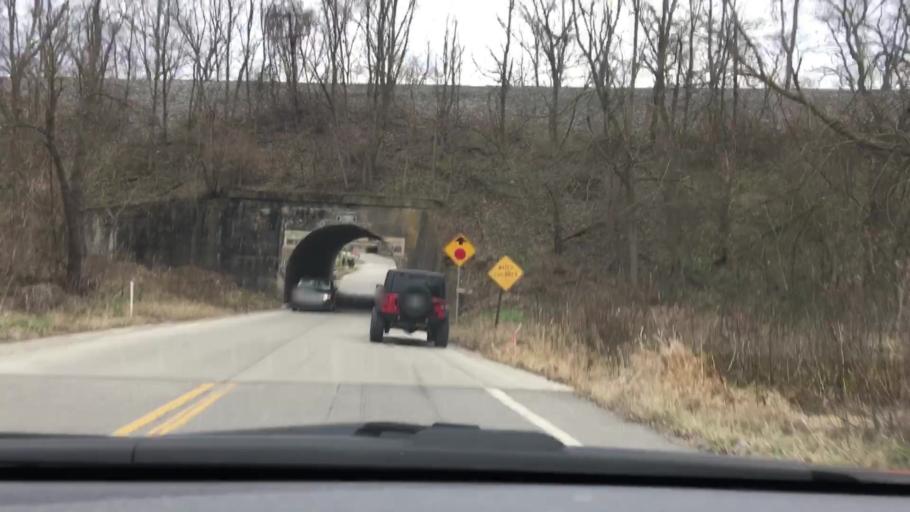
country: US
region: Pennsylvania
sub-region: Washington County
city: Cecil-Bishop
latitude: 40.3227
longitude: -80.2327
